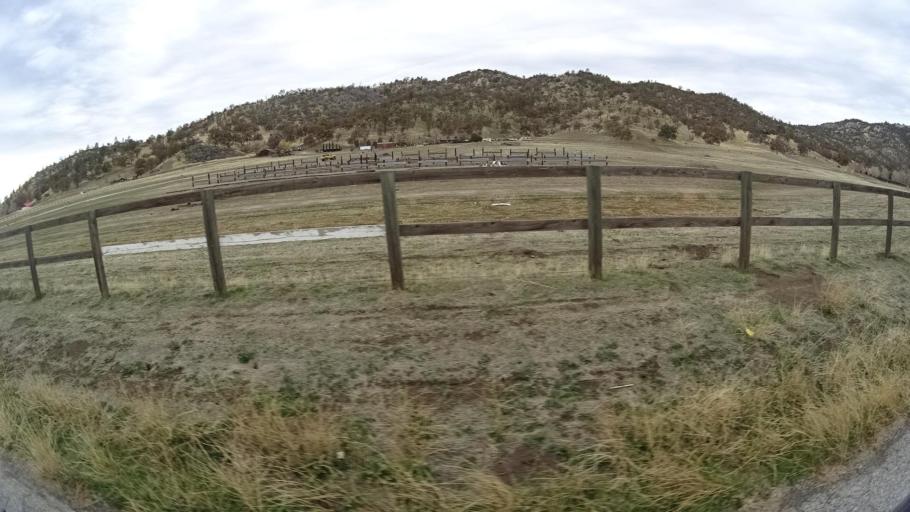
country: US
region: California
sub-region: Kern County
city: Stallion Springs
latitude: 35.1140
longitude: -118.6279
